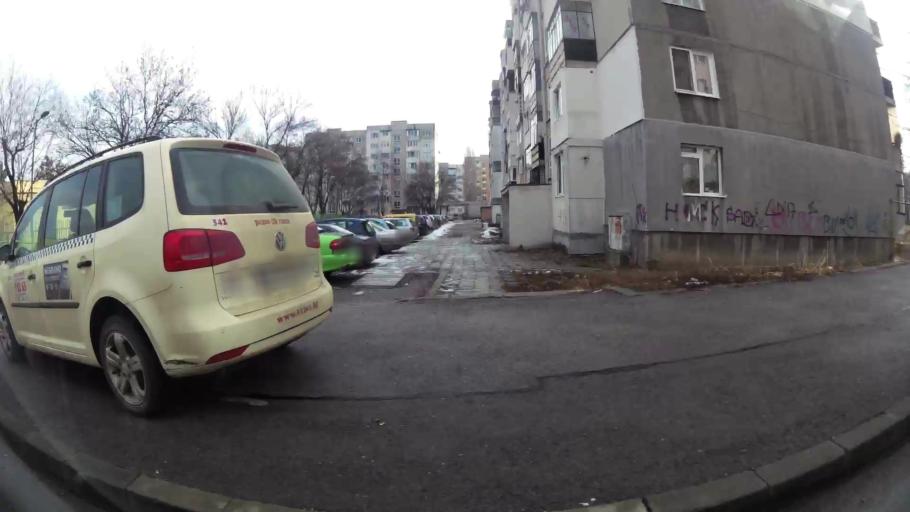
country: BG
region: Sofiya
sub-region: Obshtina Bozhurishte
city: Bozhurishte
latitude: 42.7214
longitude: 23.2438
